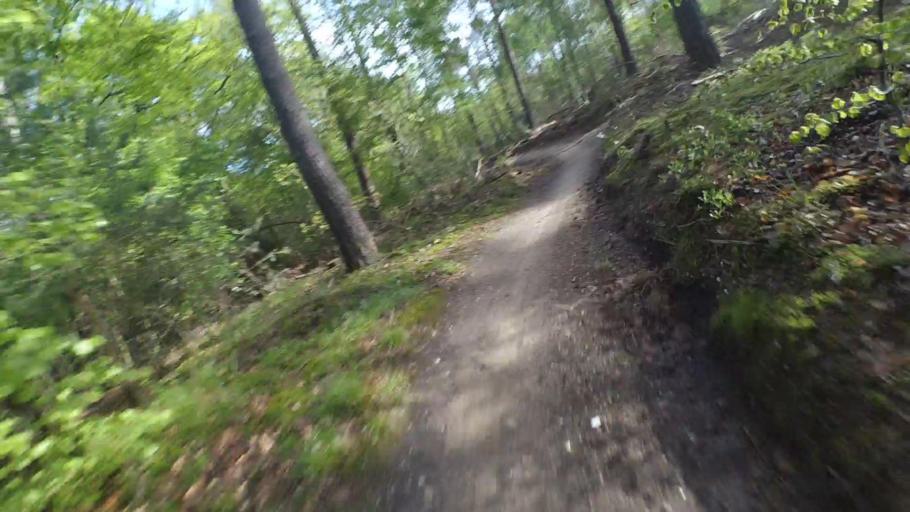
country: NL
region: Utrecht
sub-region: Gemeente Utrechtse Heuvelrug
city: Driebergen-Rijsenburg
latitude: 52.0912
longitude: 5.3050
